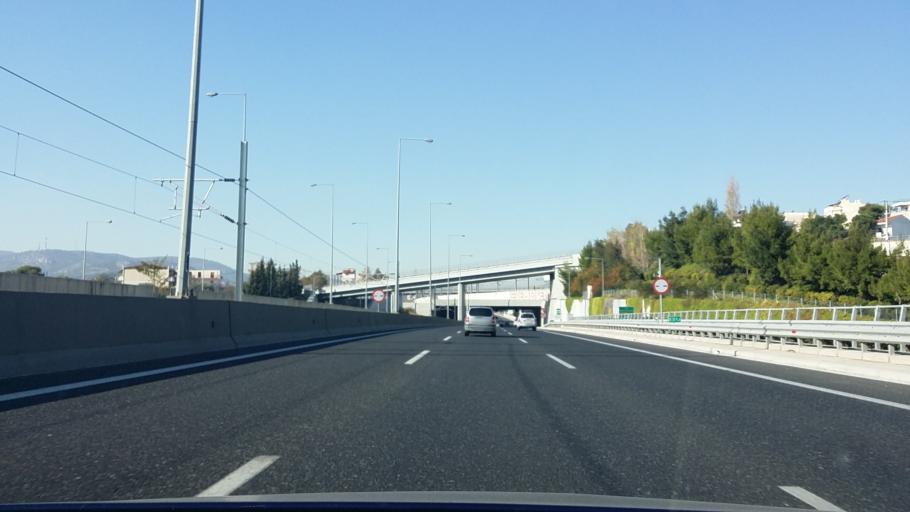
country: GR
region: Attica
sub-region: Nomarchia Dytikis Attikis
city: Zefyri
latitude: 38.0672
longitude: 23.7313
